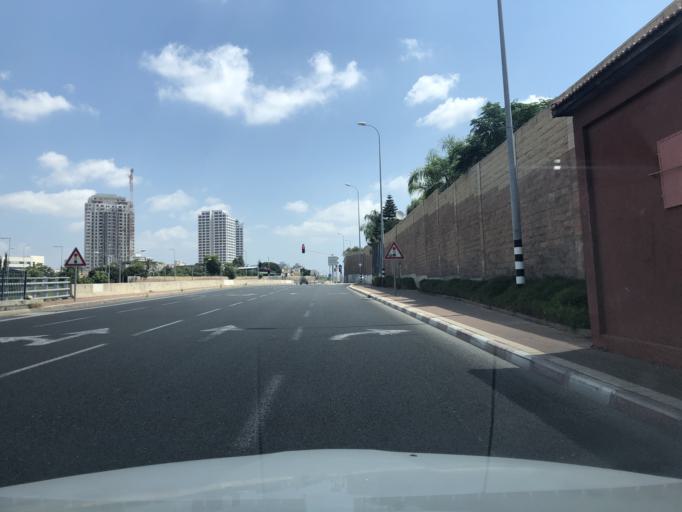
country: IL
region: Tel Aviv
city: Giv`at Shemu'el
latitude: 32.0666
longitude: 34.8481
